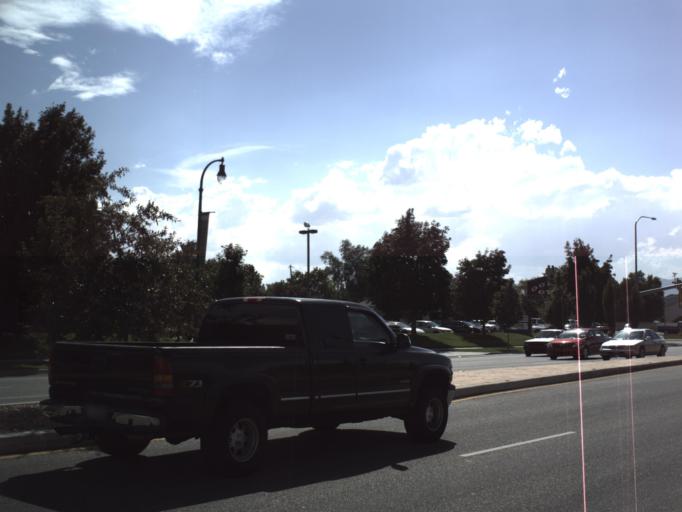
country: US
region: Utah
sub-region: Utah County
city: Orem
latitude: 40.3121
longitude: -111.6919
